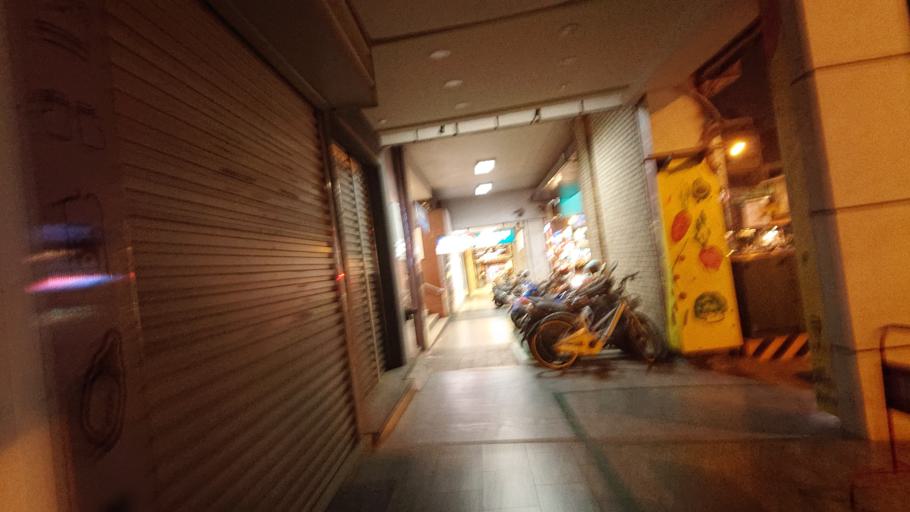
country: TW
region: Taiwan
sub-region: Tainan
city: Tainan
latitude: 22.9940
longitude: 120.2008
